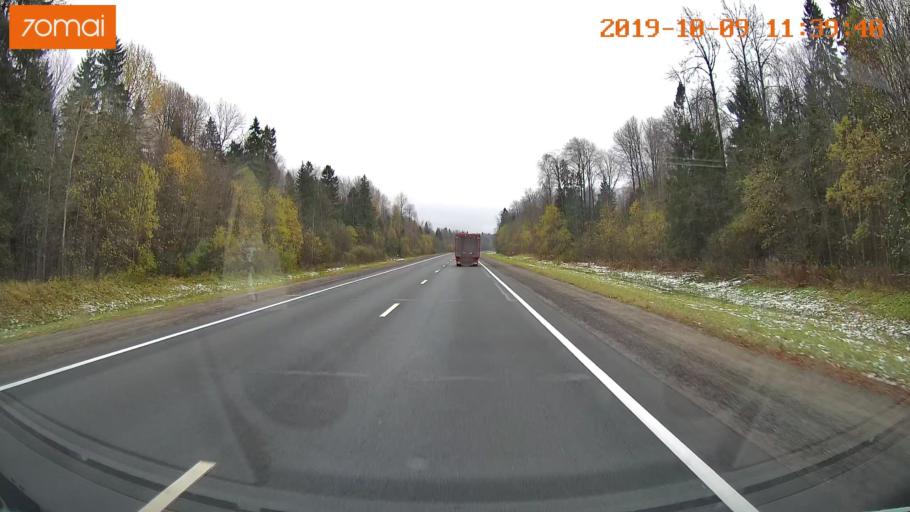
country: RU
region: Vologda
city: Gryazovets
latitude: 58.9533
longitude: 40.1682
